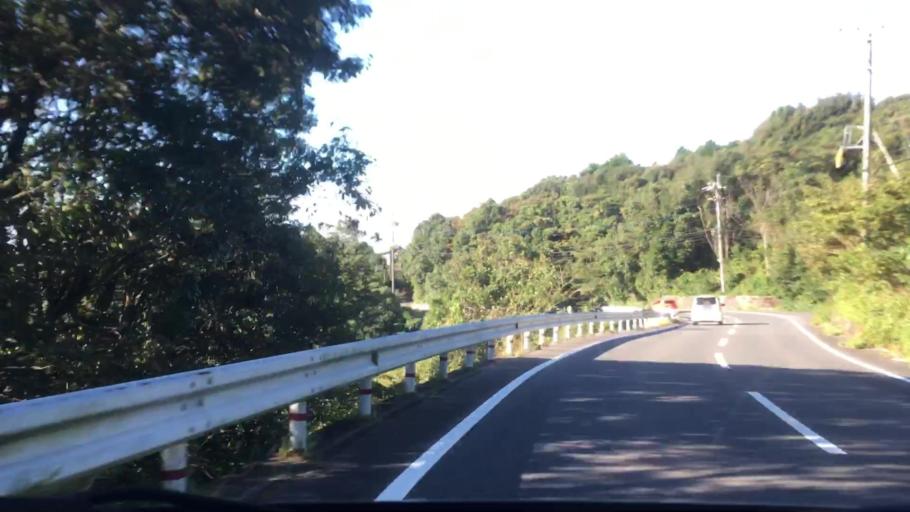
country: JP
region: Nagasaki
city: Sasebo
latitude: 32.9580
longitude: 129.6795
